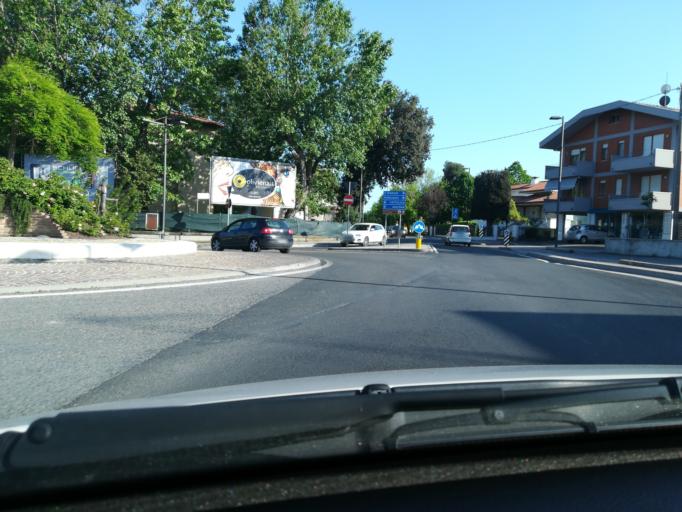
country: IT
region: Emilia-Romagna
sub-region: Provincia di Rimini
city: Riccione
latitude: 43.9878
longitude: 12.6720
